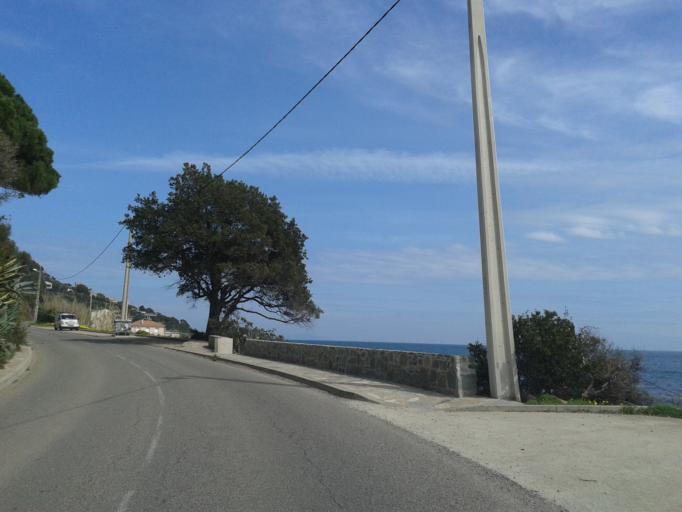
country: FR
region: Corsica
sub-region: Departement de la Haute-Corse
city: Brando
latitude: 42.7767
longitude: 9.4776
